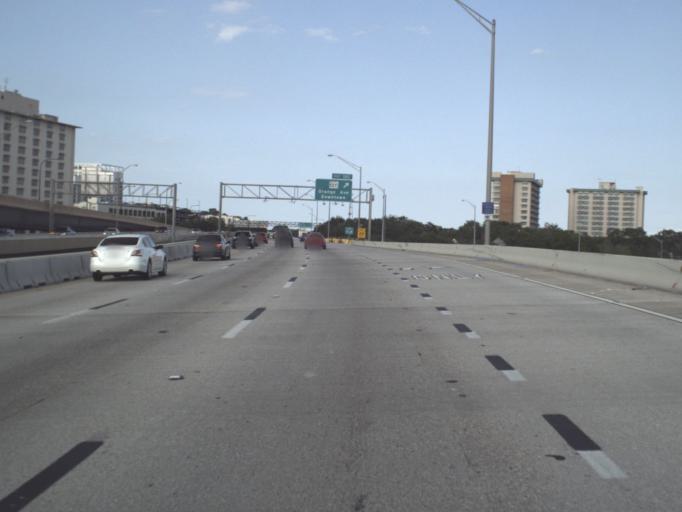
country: US
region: Florida
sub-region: Orange County
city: Orlando
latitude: 28.5354
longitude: -81.3792
